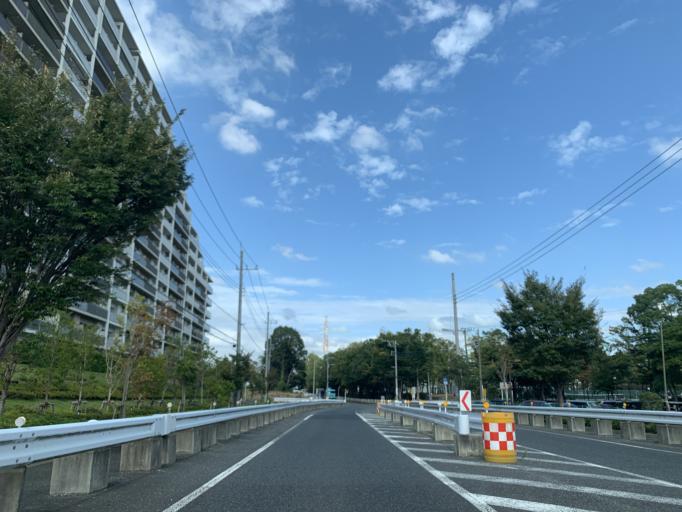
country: JP
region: Chiba
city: Nagareyama
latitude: 35.8566
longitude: 139.9170
